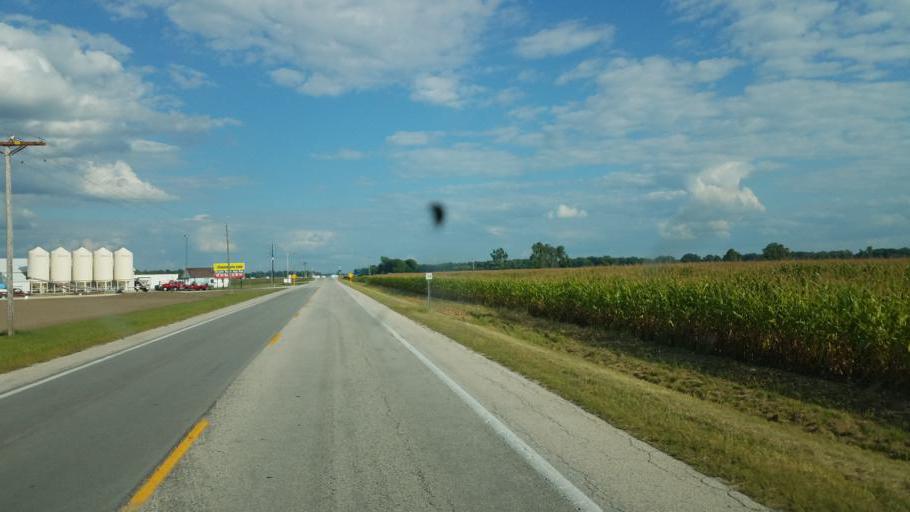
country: US
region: Ohio
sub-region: Wood County
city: Pemberville
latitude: 41.3446
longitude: -83.4453
